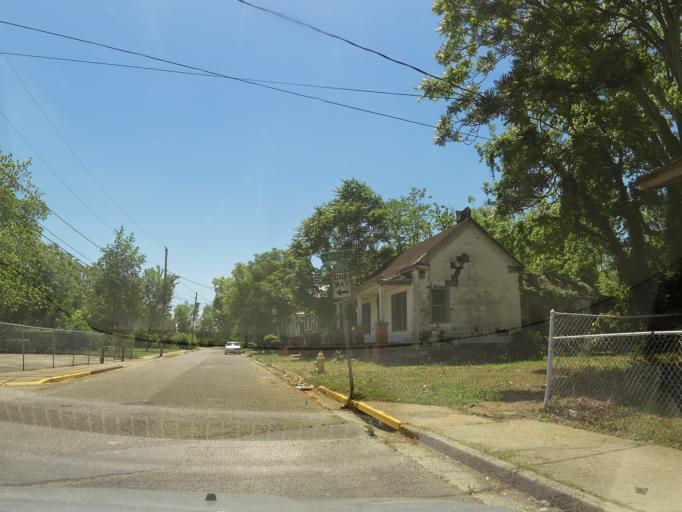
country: US
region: Georgia
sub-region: Richmond County
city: Augusta
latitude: 33.4564
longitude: -81.9790
